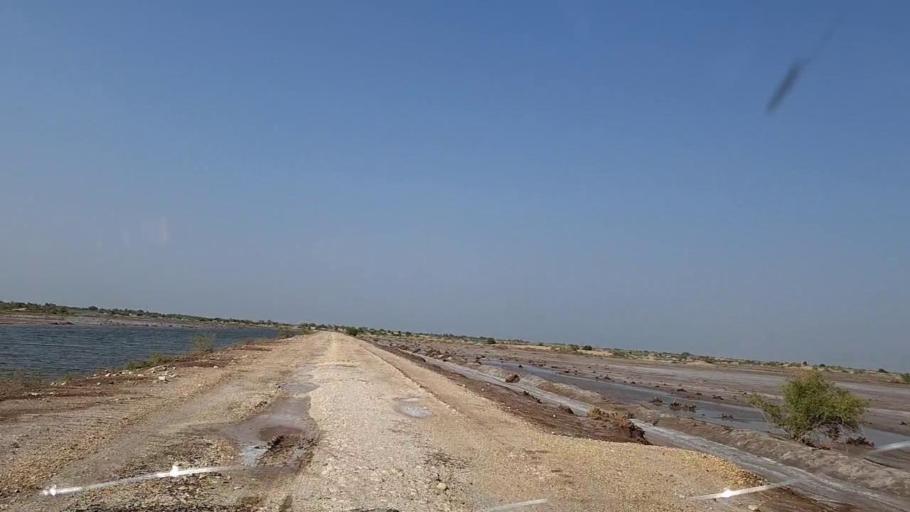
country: PK
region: Sindh
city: Khanpur
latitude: 27.6918
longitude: 69.3827
